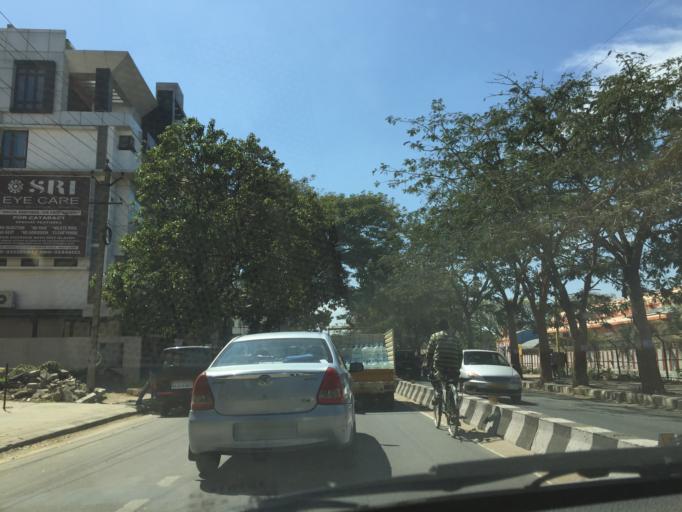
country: IN
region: Karnataka
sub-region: Bangalore Urban
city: Bangalore
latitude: 13.0201
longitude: 77.6285
